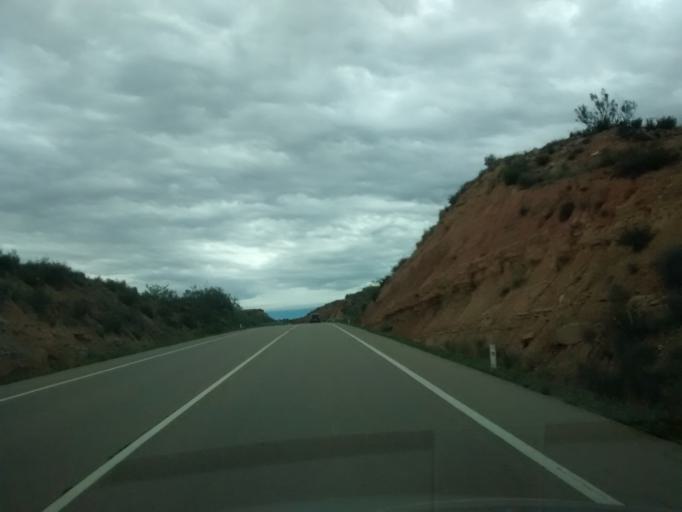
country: ES
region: Aragon
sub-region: Provincia de Zaragoza
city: Caspe
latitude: 41.2021
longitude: 0.0410
